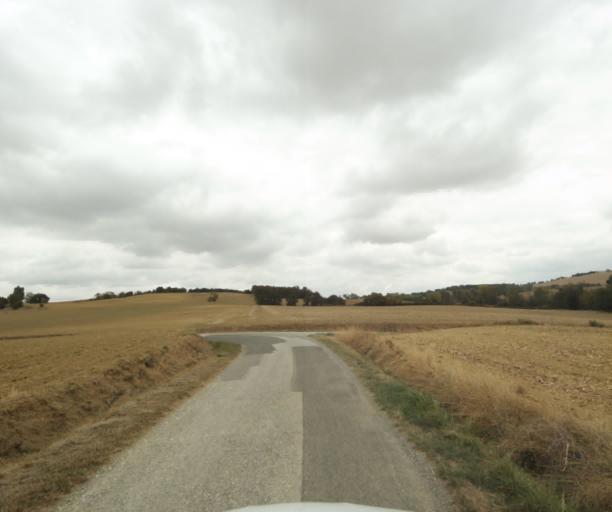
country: FR
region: Midi-Pyrenees
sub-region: Departement de la Haute-Garonne
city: Villefranche-de-Lauragais
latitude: 43.4170
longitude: 1.7462
